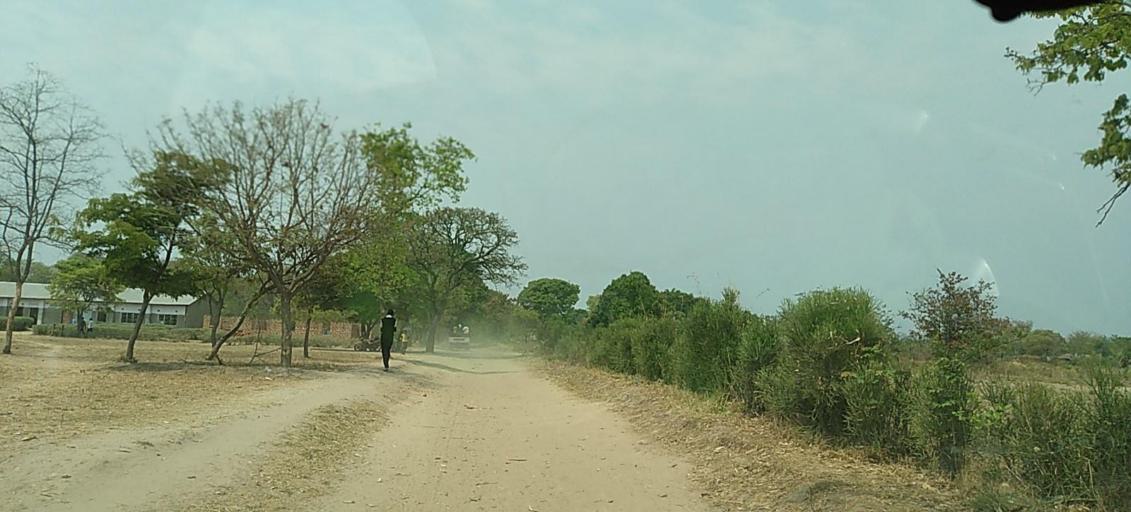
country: ZM
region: North-Western
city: Kabompo
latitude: -13.4965
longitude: 24.4661
